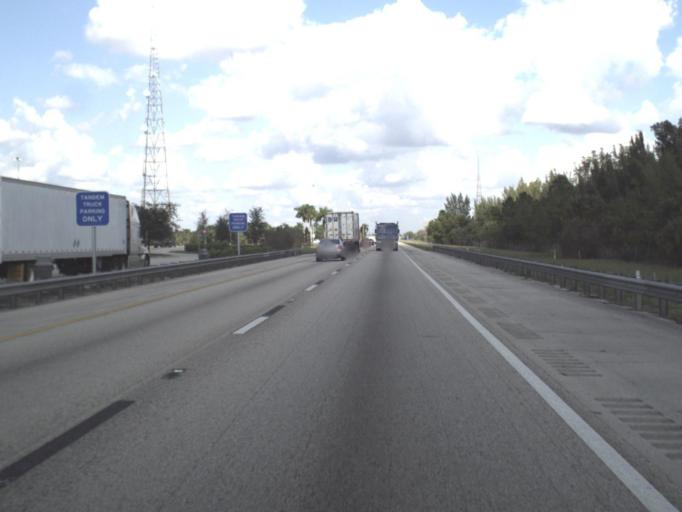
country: US
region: Florida
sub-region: Palm Beach County
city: Greenacres City
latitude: 26.6340
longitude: -80.1738
